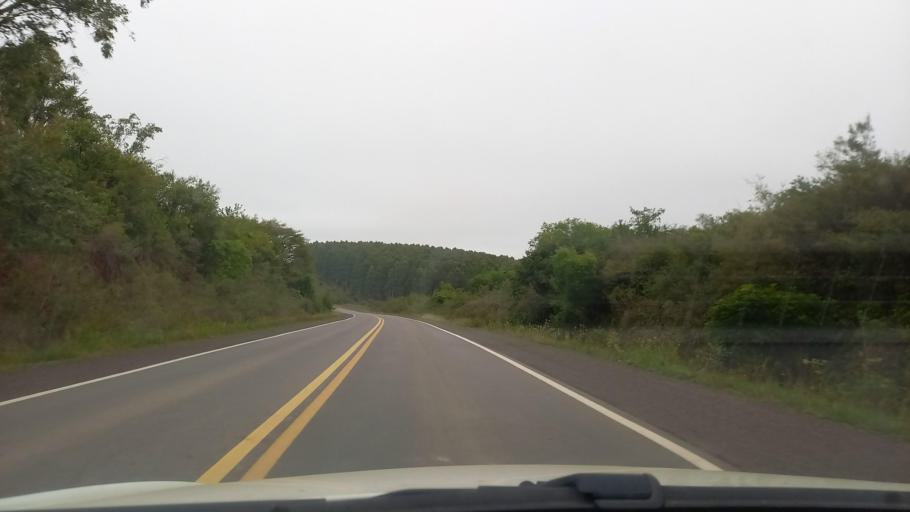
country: BR
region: Rio Grande do Sul
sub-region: Cacequi
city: Cacequi
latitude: -30.0388
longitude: -54.5905
